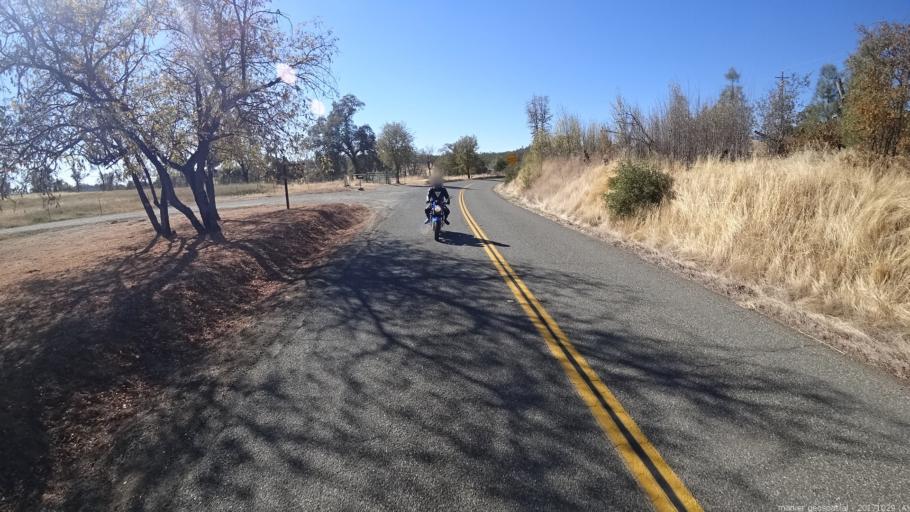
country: US
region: California
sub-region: Shasta County
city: Shasta
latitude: 40.4741
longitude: -122.6137
